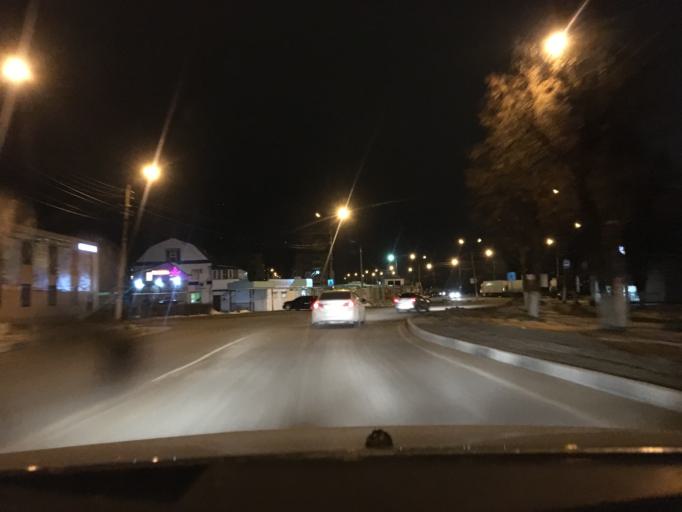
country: RU
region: Tula
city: Shchekino
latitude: 54.0203
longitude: 37.5032
